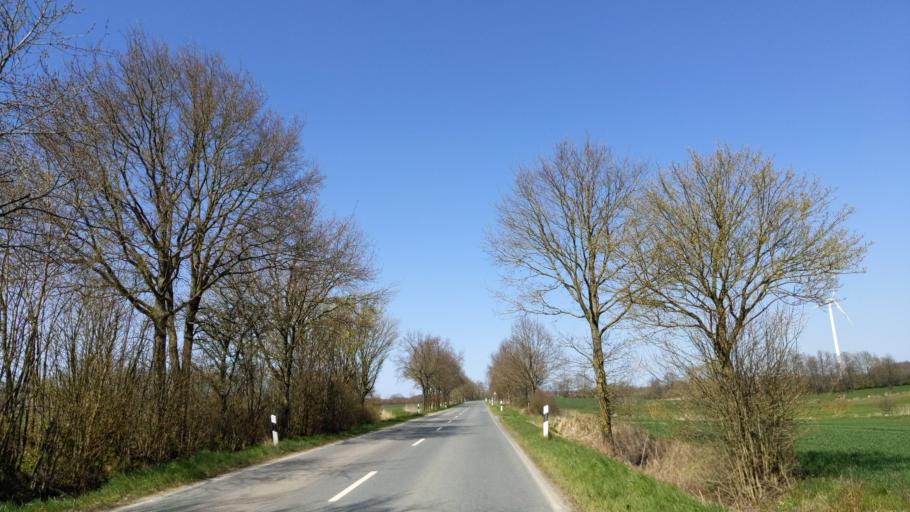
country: DE
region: Schleswig-Holstein
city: Ahrensbok
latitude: 54.0032
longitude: 10.6567
